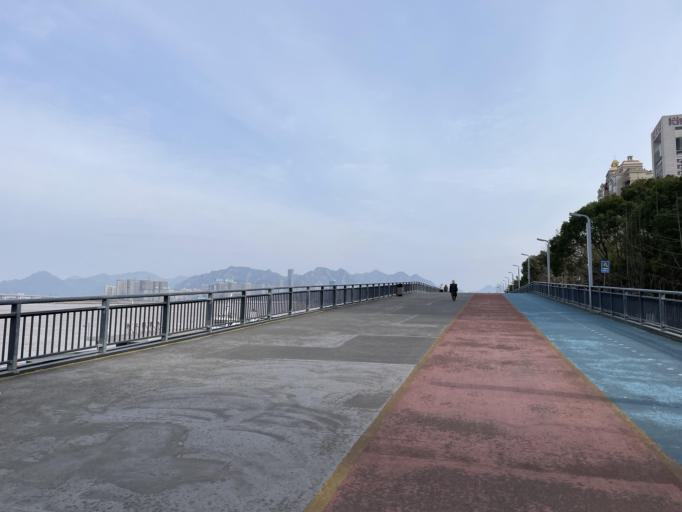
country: CN
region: Zhejiang Sheng
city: Wuma
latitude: 28.0287
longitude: 120.6556
